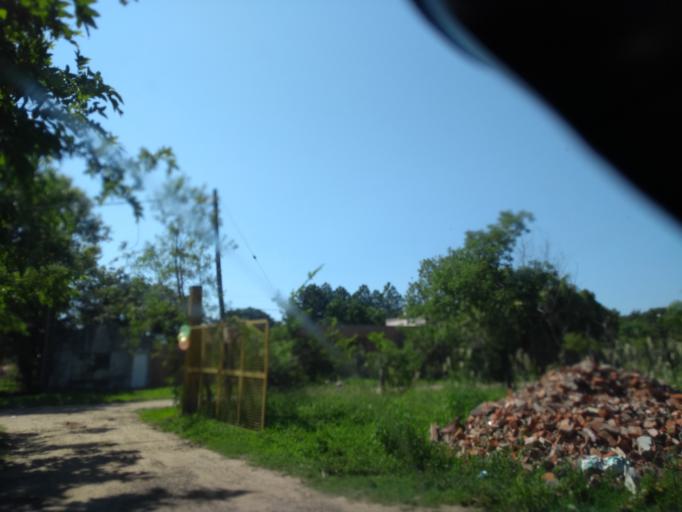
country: AR
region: Chaco
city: Resistencia
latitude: -27.4344
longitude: -58.9453
